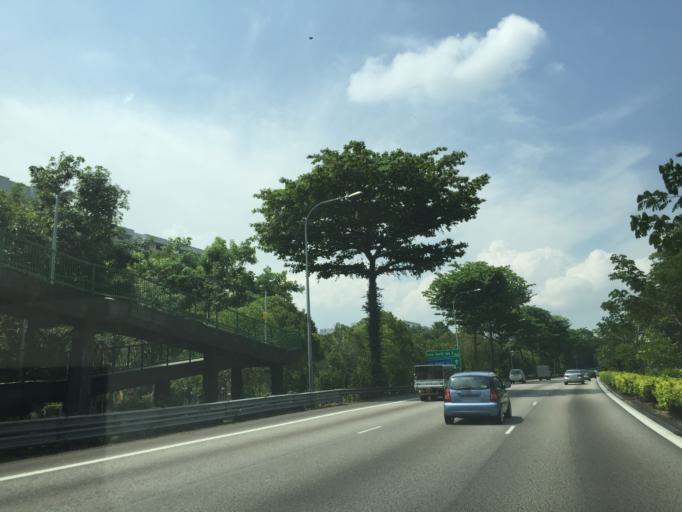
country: SG
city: Singapore
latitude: 1.3349
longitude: 103.9252
